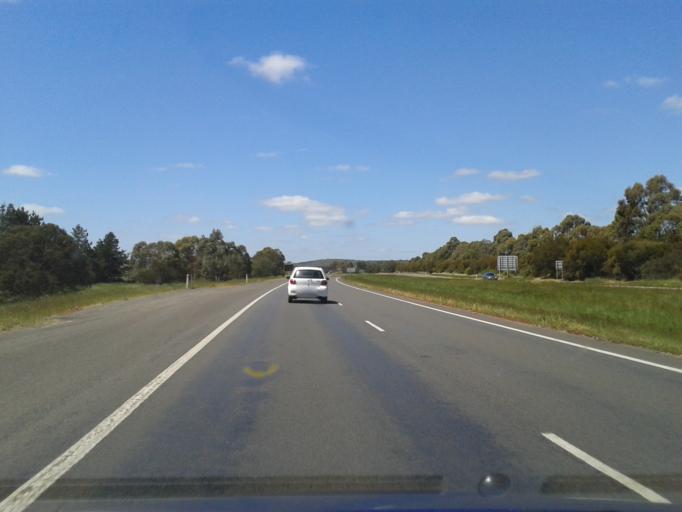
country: AU
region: Victoria
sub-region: Ballarat North
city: Lake Wendouree
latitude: -37.5180
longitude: 143.8356
